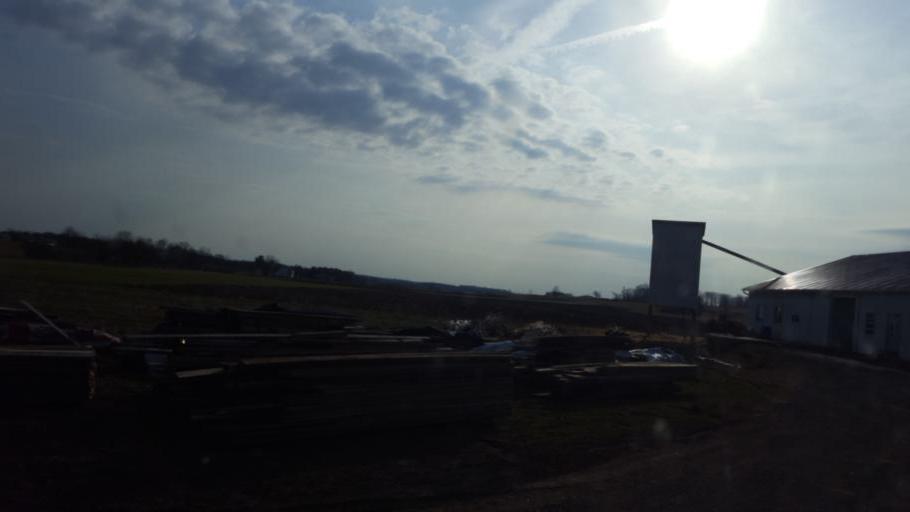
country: US
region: Ohio
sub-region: Knox County
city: Fredericktown
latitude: 40.5227
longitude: -82.6213
